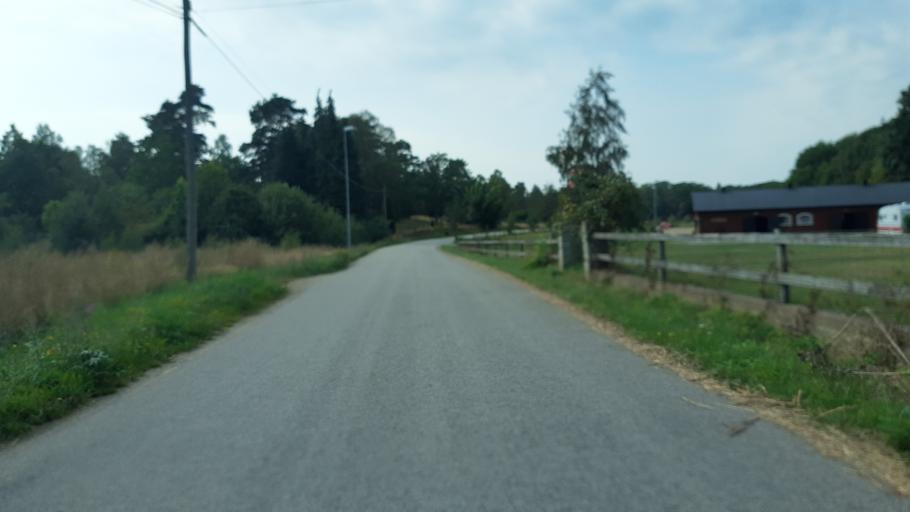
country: SE
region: Blekinge
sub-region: Karlskrona Kommun
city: Nattraby
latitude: 56.1763
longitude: 15.4829
